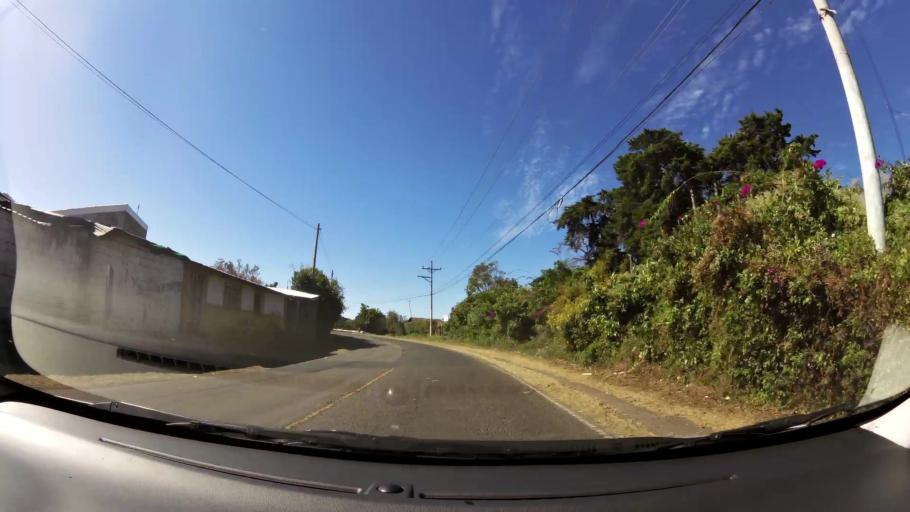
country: SV
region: Ahuachapan
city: Concepcion de Ataco
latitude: 13.8623
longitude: -89.8047
